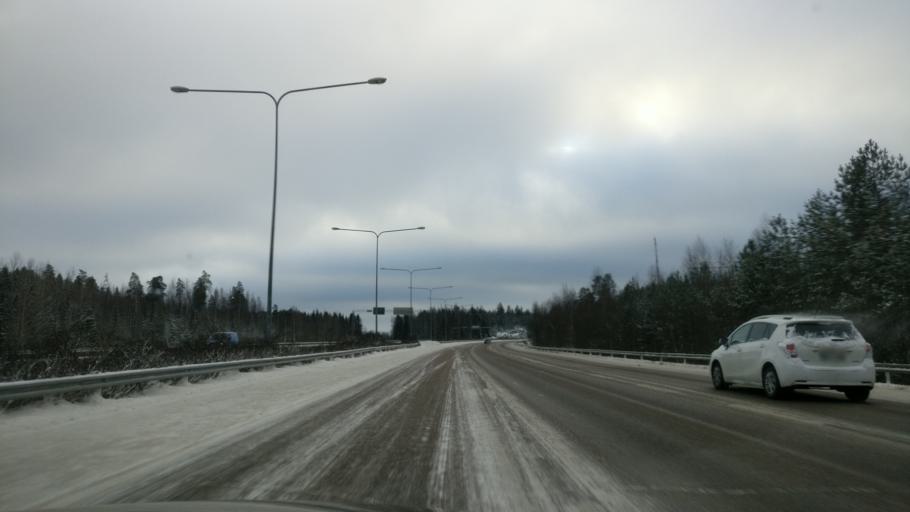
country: FI
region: Paijanne Tavastia
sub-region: Lahti
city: Lahti
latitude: 60.9801
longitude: 25.7313
